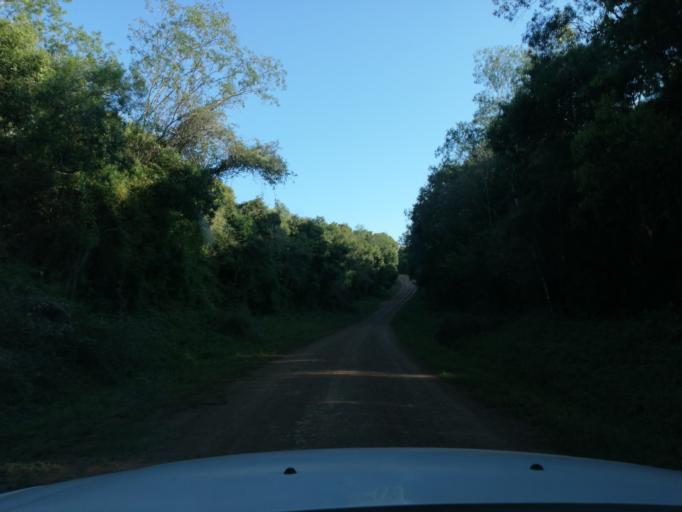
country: AR
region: Misiones
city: Cerro Cora
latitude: -27.6105
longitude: -55.7047
